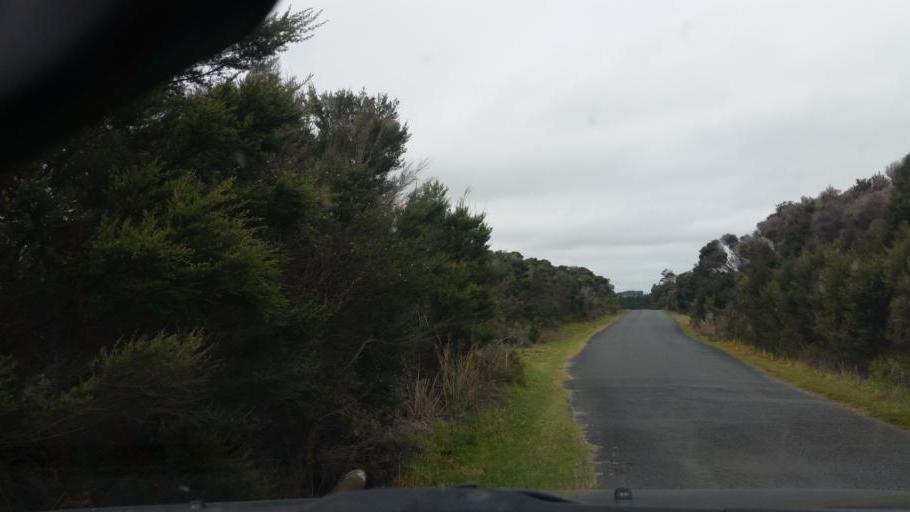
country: NZ
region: Northland
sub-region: Kaipara District
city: Dargaville
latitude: -35.8122
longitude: 173.6521
